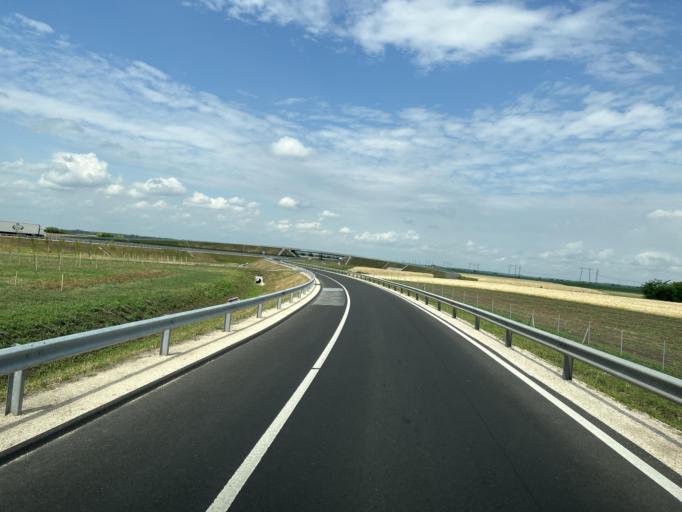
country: HU
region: Pest
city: Abony
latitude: 47.2089
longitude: 20.0721
